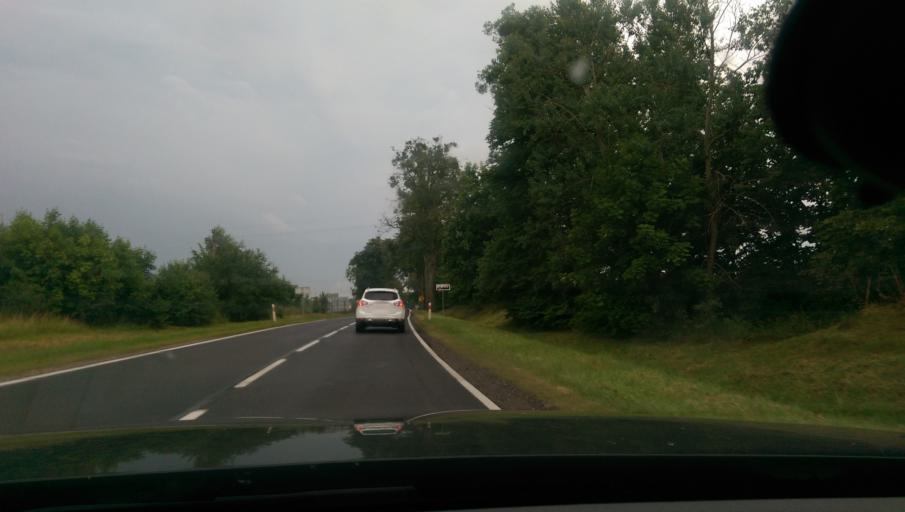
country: PL
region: Warmian-Masurian Voivodeship
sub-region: Powiat szczycienski
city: Szczytno
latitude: 53.5508
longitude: 20.9887
